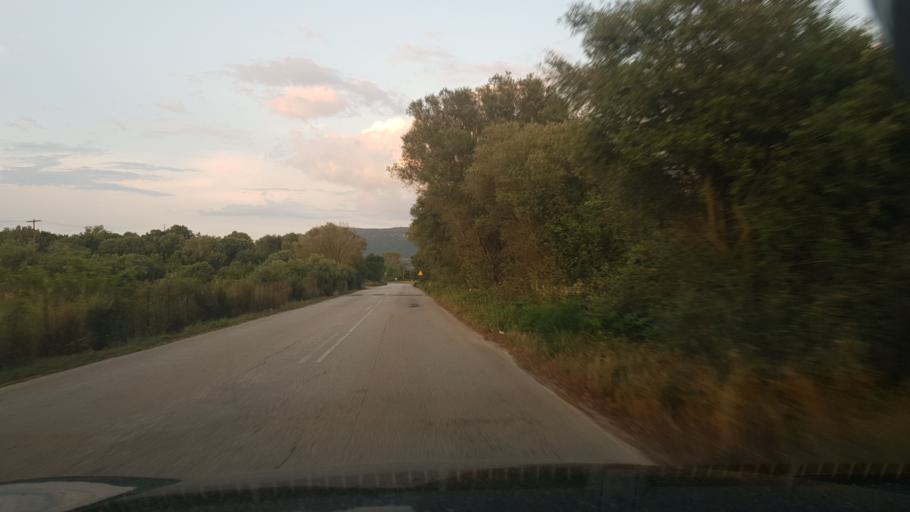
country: GR
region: West Greece
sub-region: Nomos Aitolias kai Akarnanias
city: Vonitsa
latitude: 38.8832
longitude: 20.8374
